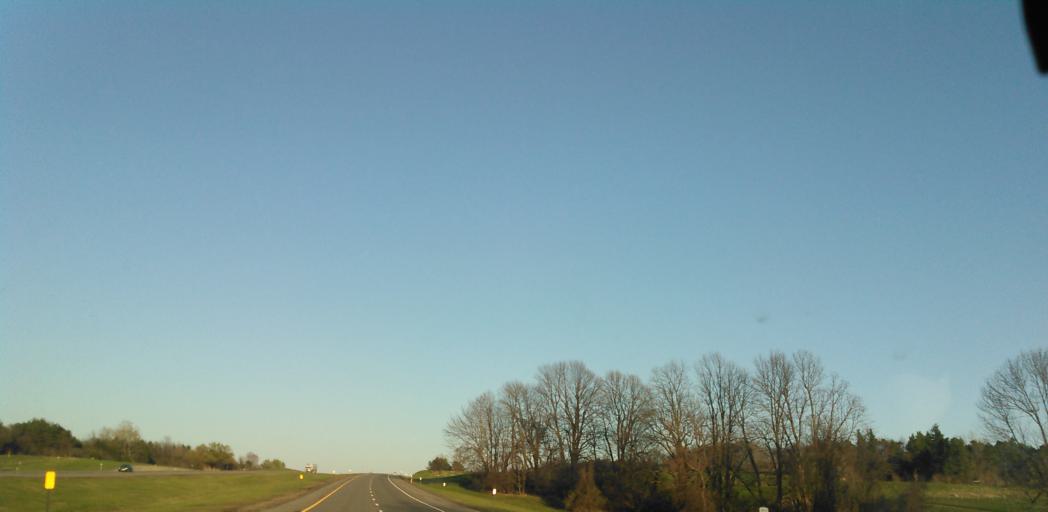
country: US
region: New York
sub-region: Monroe County
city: Pittsford
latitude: 43.0434
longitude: -77.5530
